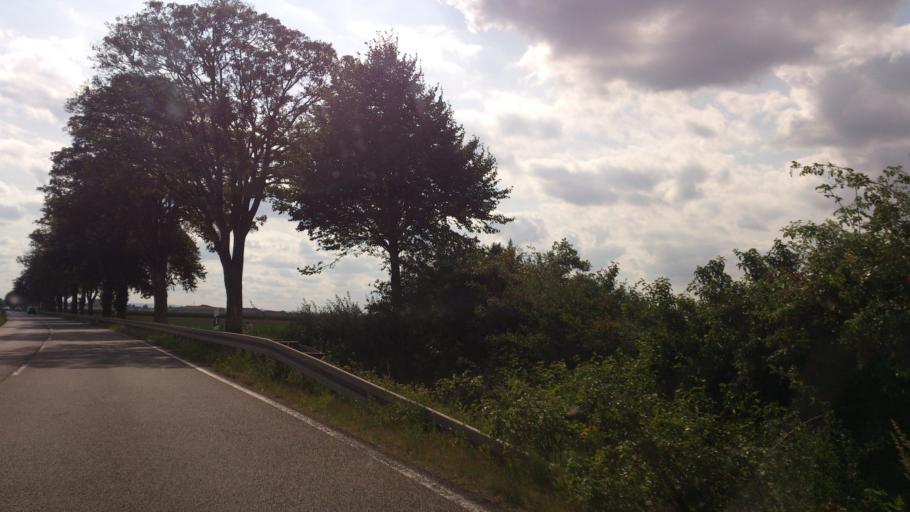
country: DE
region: North Rhine-Westphalia
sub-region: Regierungsbezirk Koln
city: Erftstadt
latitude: 50.7870
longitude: 6.7458
